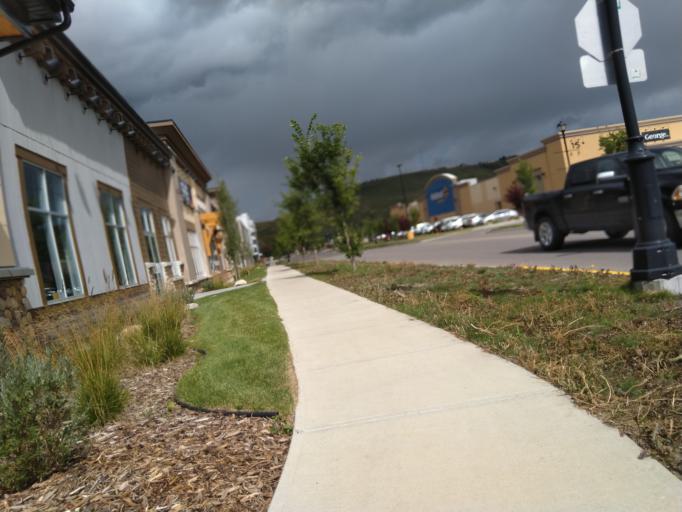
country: CA
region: Alberta
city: Cochrane
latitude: 51.1858
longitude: -114.4732
